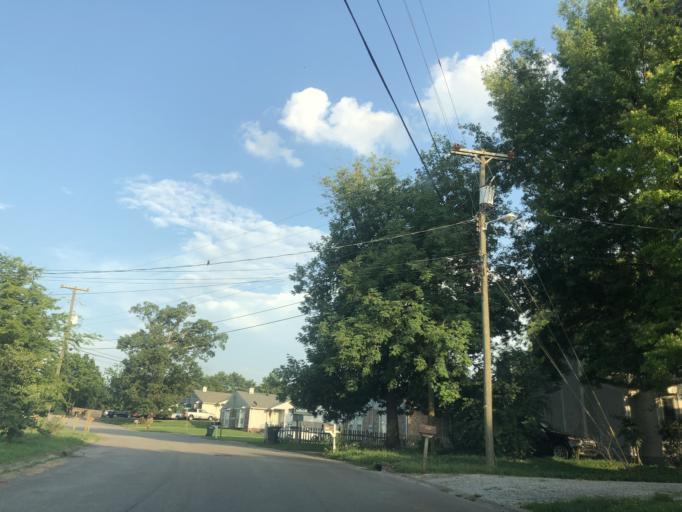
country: US
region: Tennessee
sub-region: Davidson County
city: Lakewood
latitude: 36.1456
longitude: -86.6429
